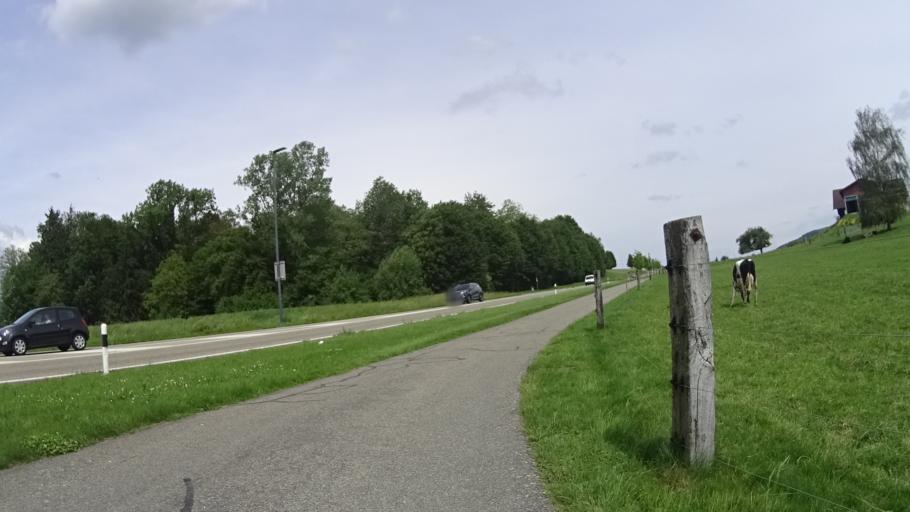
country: CH
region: Aargau
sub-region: Bezirk Rheinfelden
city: Mohlin
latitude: 47.5527
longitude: 7.8338
